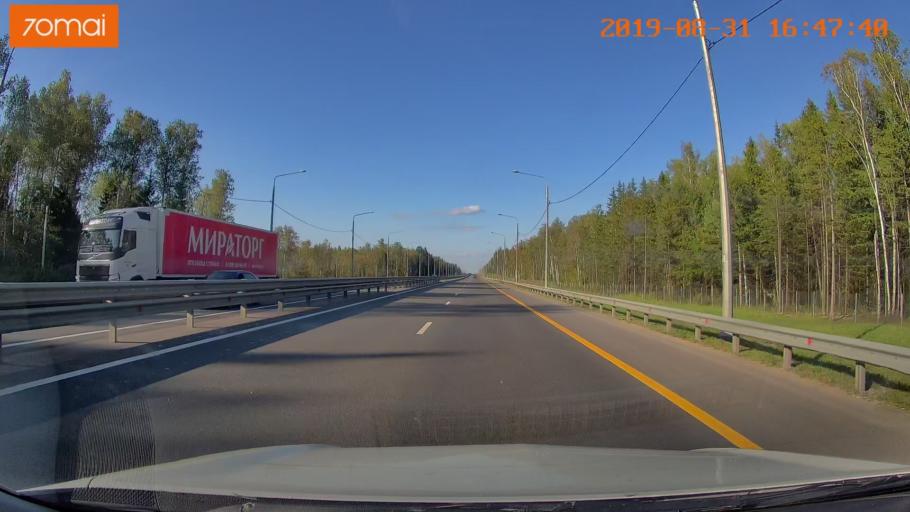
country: RU
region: Kaluga
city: Pyatovskiy
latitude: 54.6583
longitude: 36.1407
